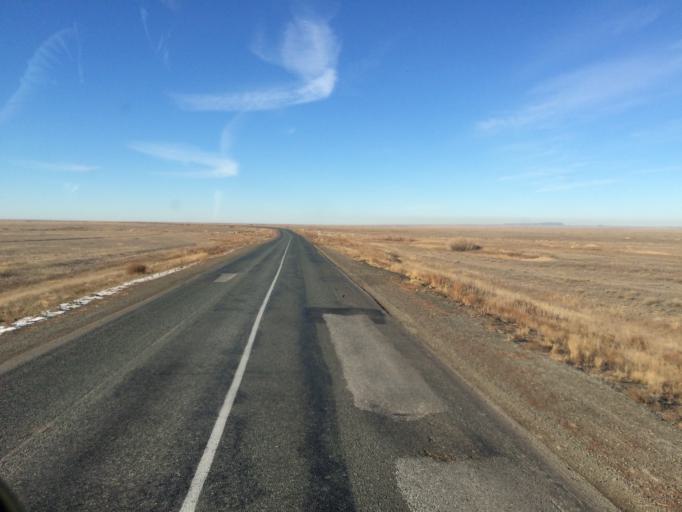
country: KZ
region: Aqtoebe
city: Khromtau
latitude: 50.1857
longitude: 58.6753
